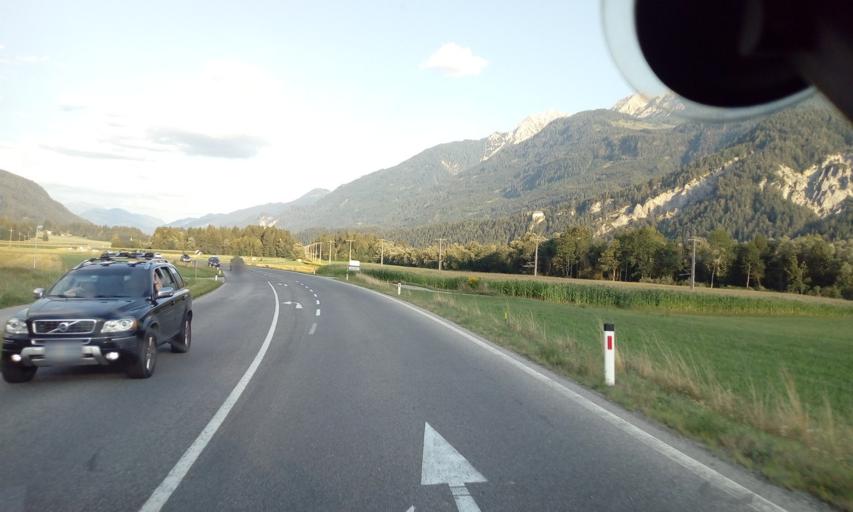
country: AT
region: Carinthia
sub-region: Politischer Bezirk Spittal an der Drau
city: Irschen
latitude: 46.7432
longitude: 13.0012
